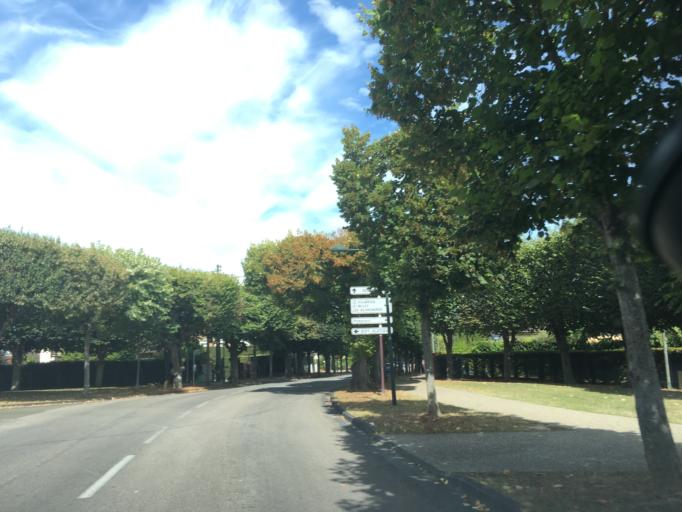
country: FR
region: Haute-Normandie
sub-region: Departement de l'Eure
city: Vernon
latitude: 49.0830
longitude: 1.4777
